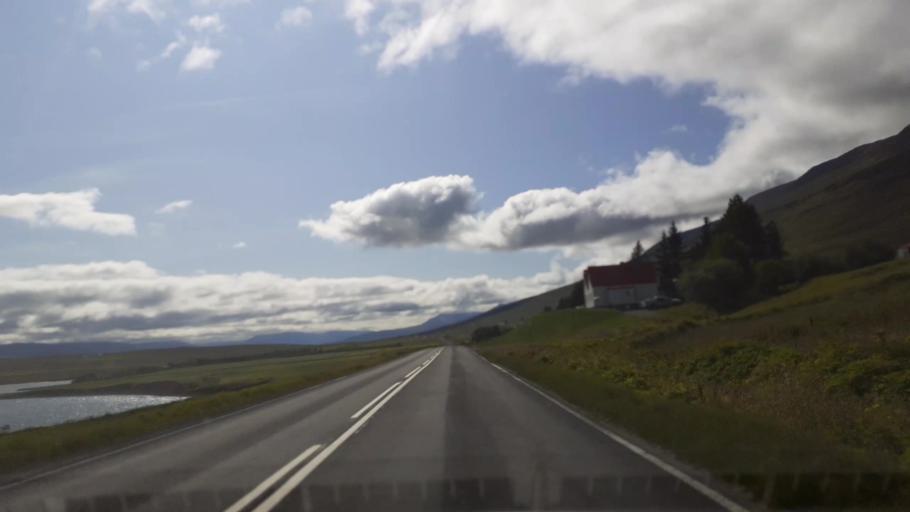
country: IS
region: Northeast
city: Akureyri
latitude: 65.8715
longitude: -18.2635
